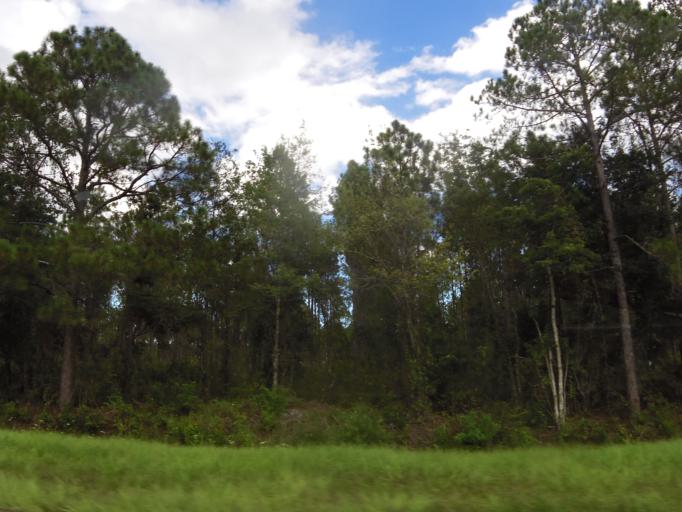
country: US
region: Florida
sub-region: Saint Johns County
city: Saint Augustine
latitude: 29.8974
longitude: -81.4949
